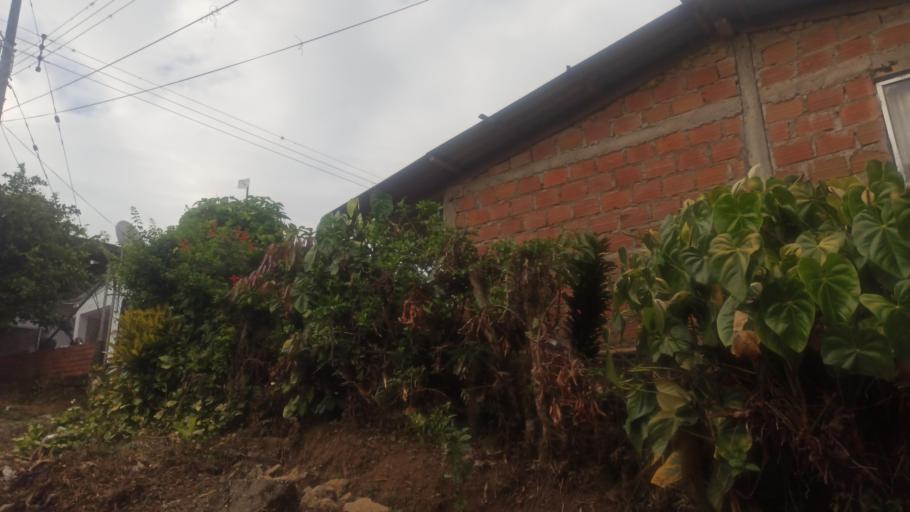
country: CO
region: Valle del Cauca
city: Jamundi
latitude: 3.1858
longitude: -76.6754
